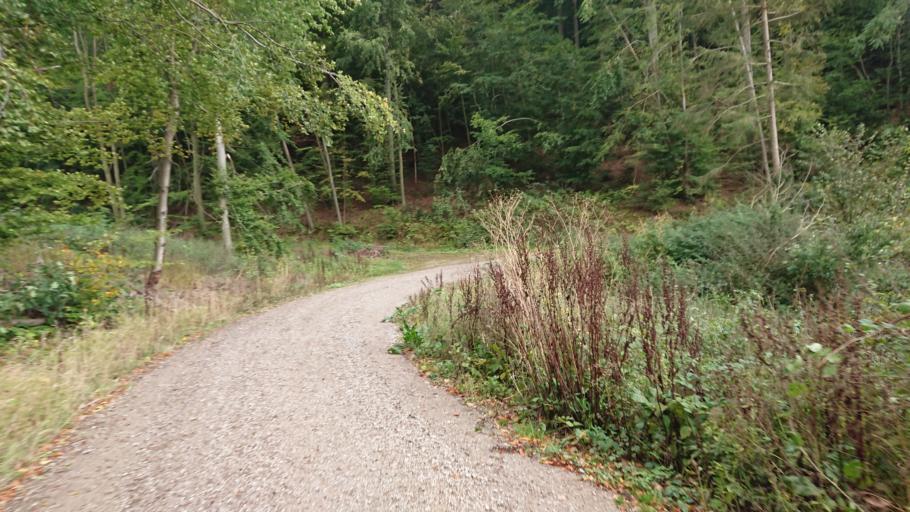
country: DE
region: Lower Saxony
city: Bovenden
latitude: 51.6067
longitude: 9.9536
